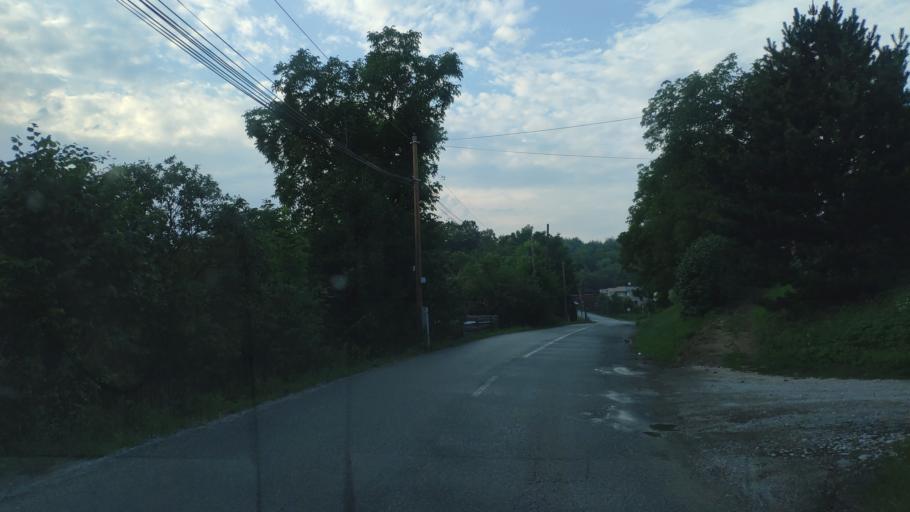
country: SK
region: Kosicky
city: Moldava nad Bodvou
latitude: 48.6866
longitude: 20.9749
